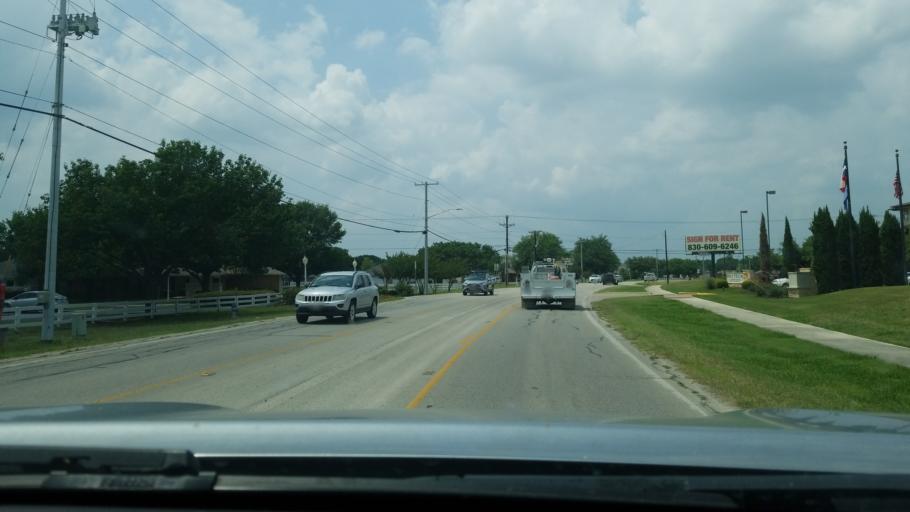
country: US
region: Texas
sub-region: Comal County
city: New Braunfels
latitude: 29.7331
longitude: -98.0983
